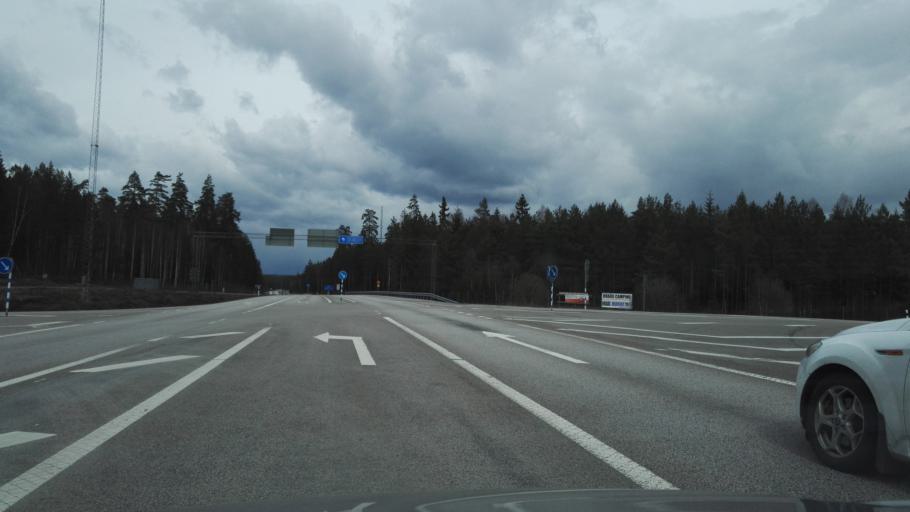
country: SE
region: Kronoberg
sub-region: Vaxjo Kommun
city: Braas
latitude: 57.0168
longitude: 15.0540
